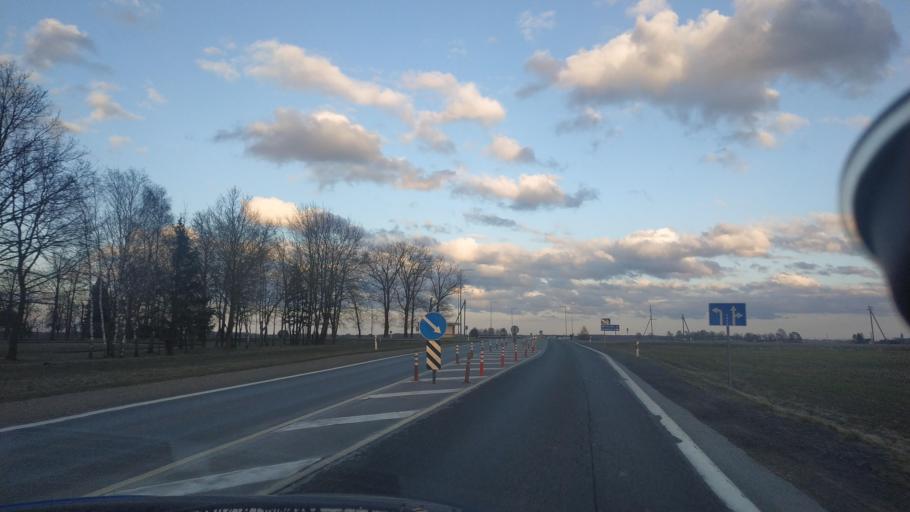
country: LT
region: Siauliu apskritis
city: Pakruojis
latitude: 55.7983
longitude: 24.0144
